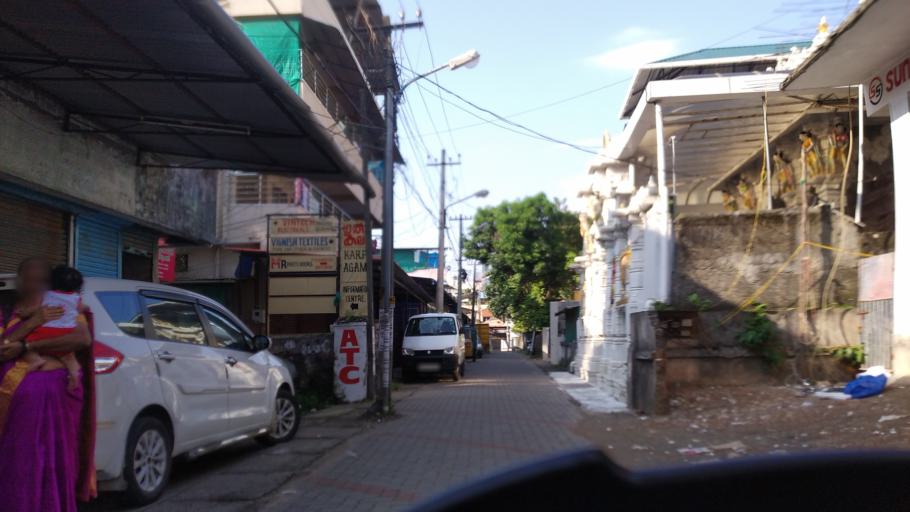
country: IN
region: Kerala
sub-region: Ernakulam
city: Cochin
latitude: 9.9807
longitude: 76.2821
